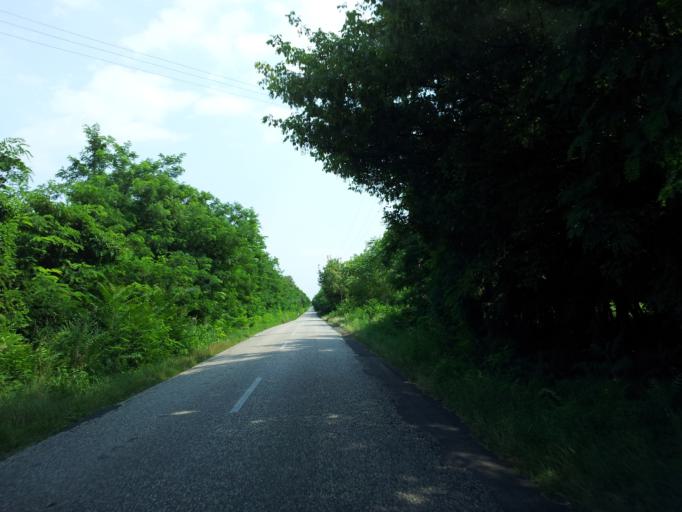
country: HU
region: Pest
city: Szigetujfalu
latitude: 47.2048
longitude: 18.9128
